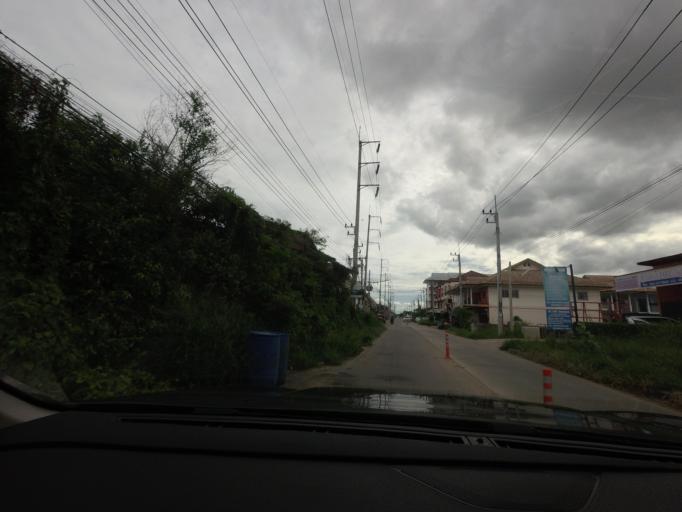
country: TH
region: Prachuap Khiri Khan
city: Hua Hin
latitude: 12.5426
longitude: 99.9511
